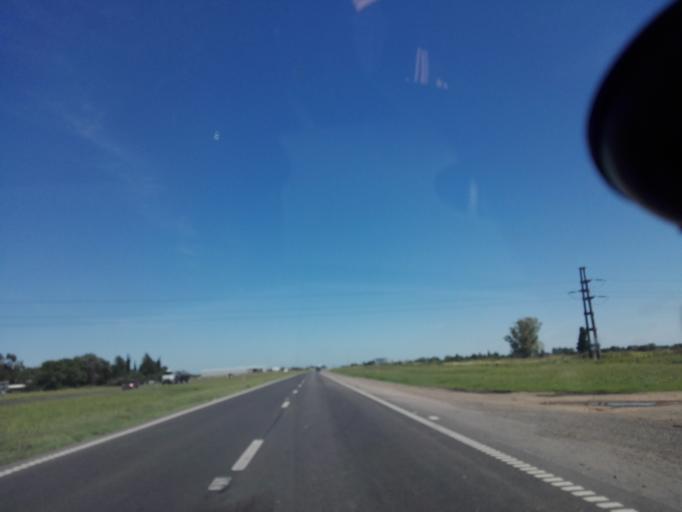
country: AR
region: Buenos Aires
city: San Nicolas de los Arroyos
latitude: -33.3801
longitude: -60.2335
